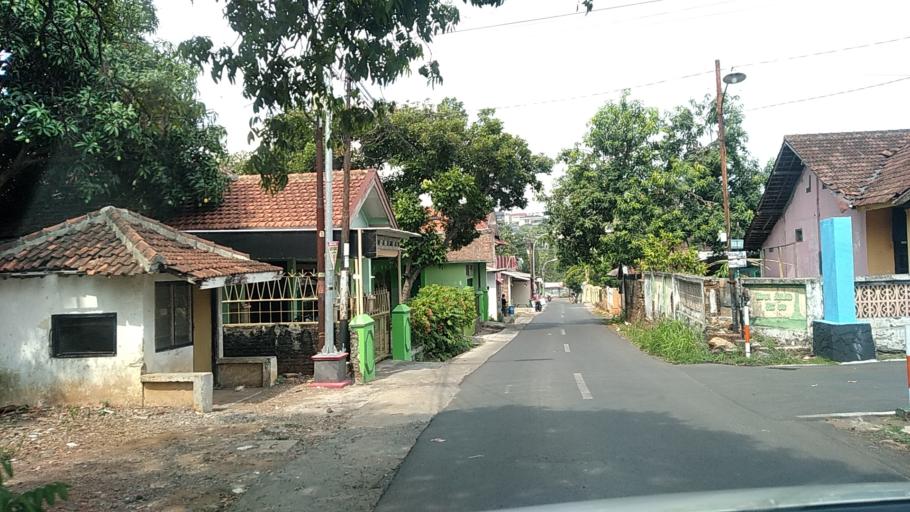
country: ID
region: Central Java
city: Semarang
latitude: -7.0340
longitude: 110.4303
